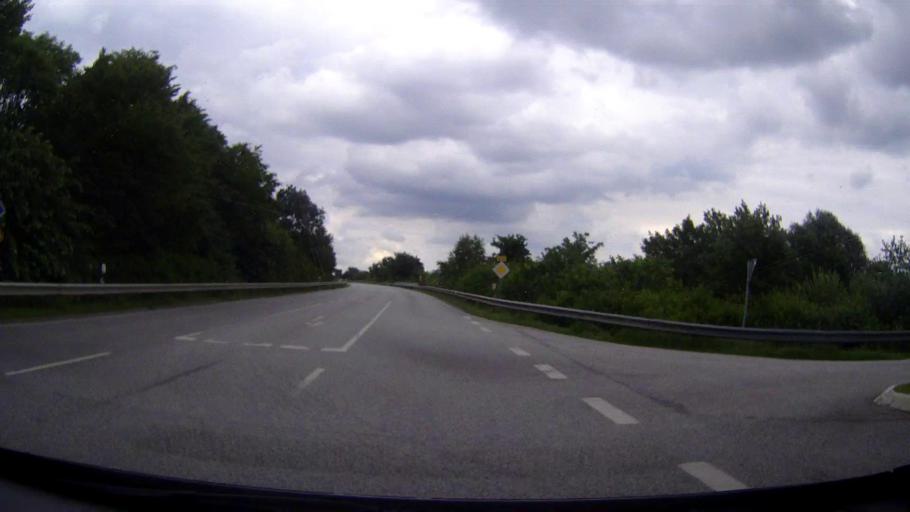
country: DE
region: Schleswig-Holstein
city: Hohenwestedt
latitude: 54.0773
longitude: 9.6492
